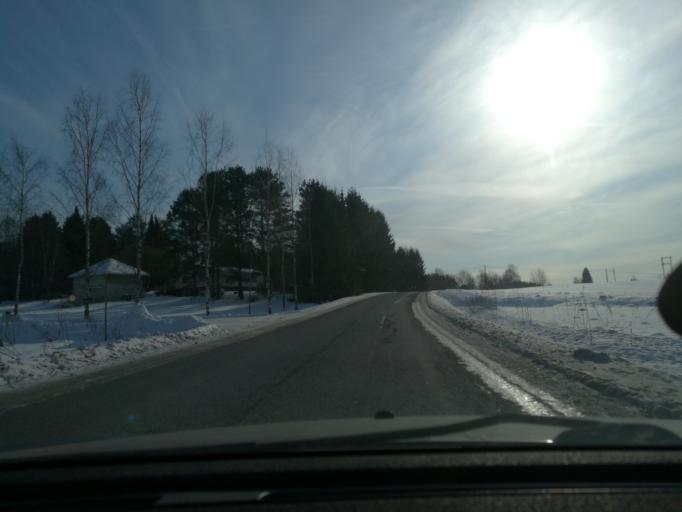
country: FI
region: Uusimaa
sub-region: Helsinki
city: Kaerkoelae
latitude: 60.5029
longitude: 23.9642
